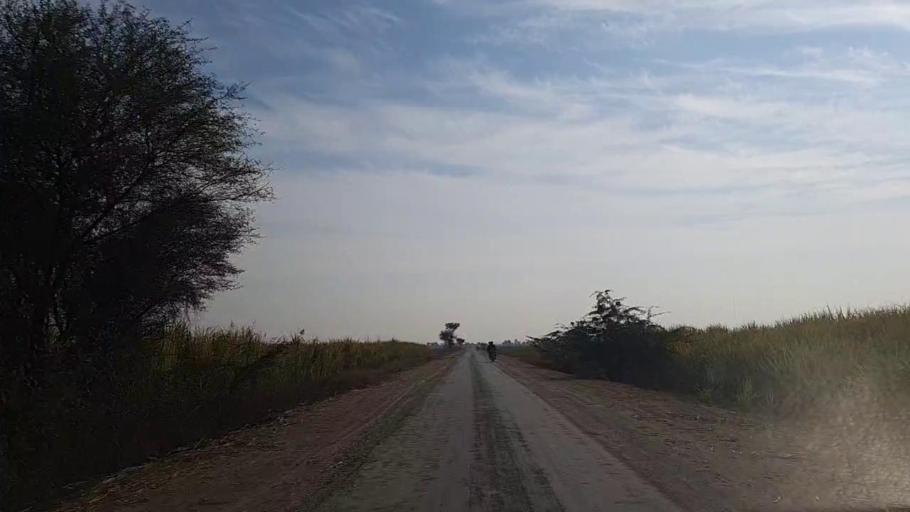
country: PK
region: Sindh
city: Daur
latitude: 26.4848
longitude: 68.4129
